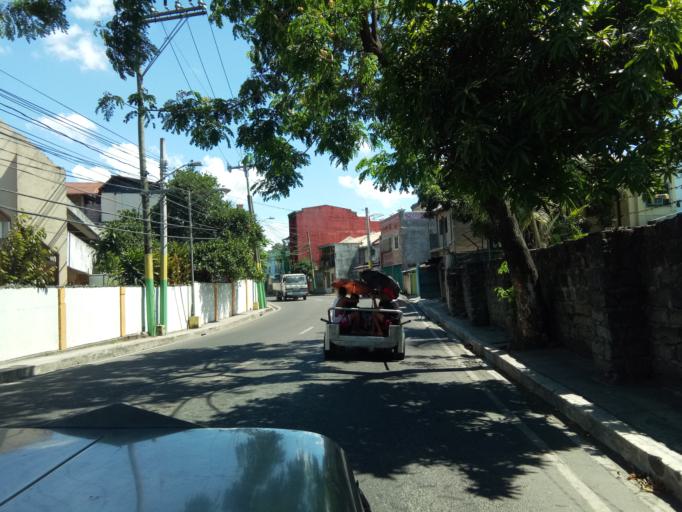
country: PH
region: Calabarzon
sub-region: Province of Cavite
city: Dasmarinas
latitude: 14.3506
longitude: 120.9448
